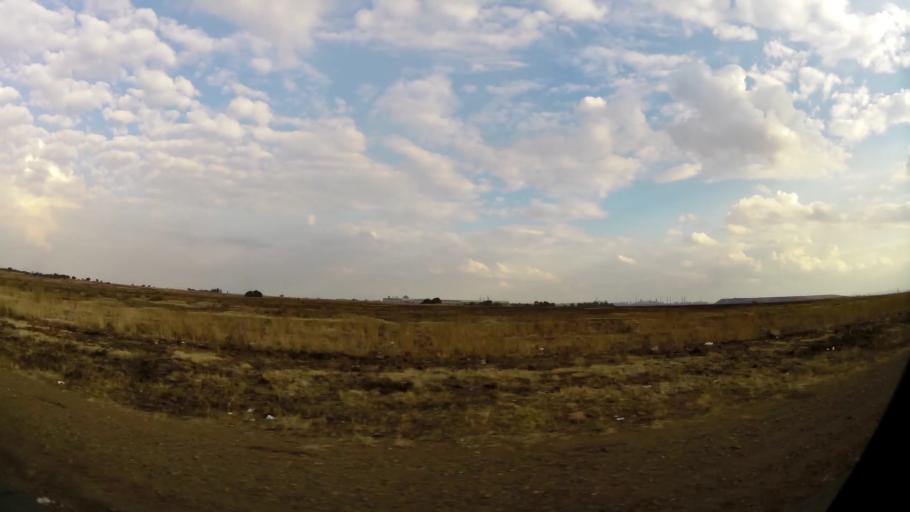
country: ZA
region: Gauteng
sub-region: Sedibeng District Municipality
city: Vanderbijlpark
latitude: -26.6184
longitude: 27.8411
